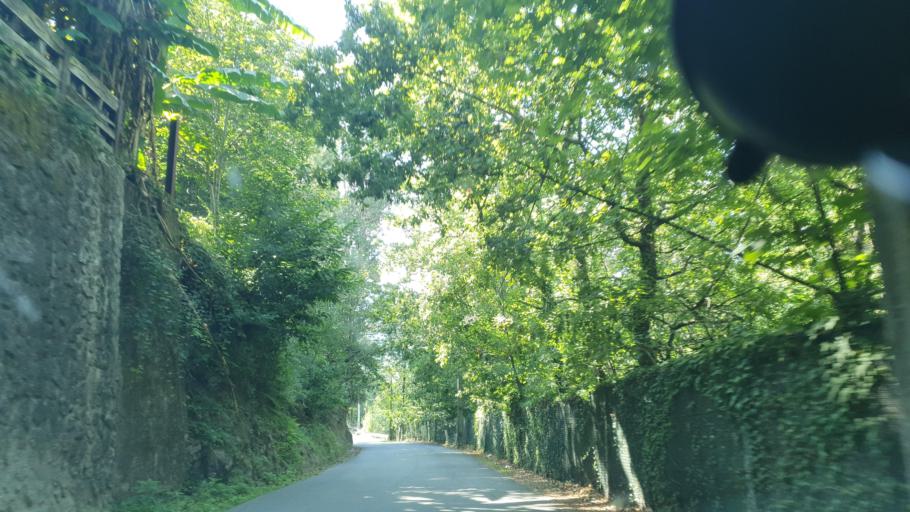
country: PT
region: Braga
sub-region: Vieira do Minho
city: Real
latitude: 41.6702
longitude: -8.1756
